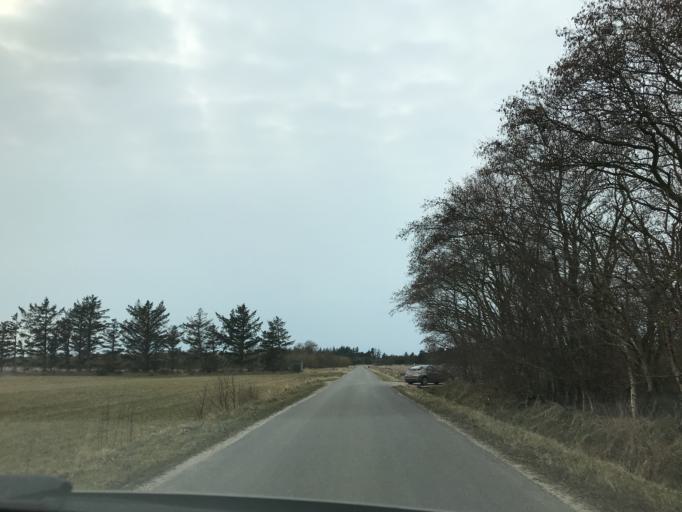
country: DK
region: South Denmark
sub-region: Varde Kommune
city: Oksbol
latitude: 55.8179
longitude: 8.2376
